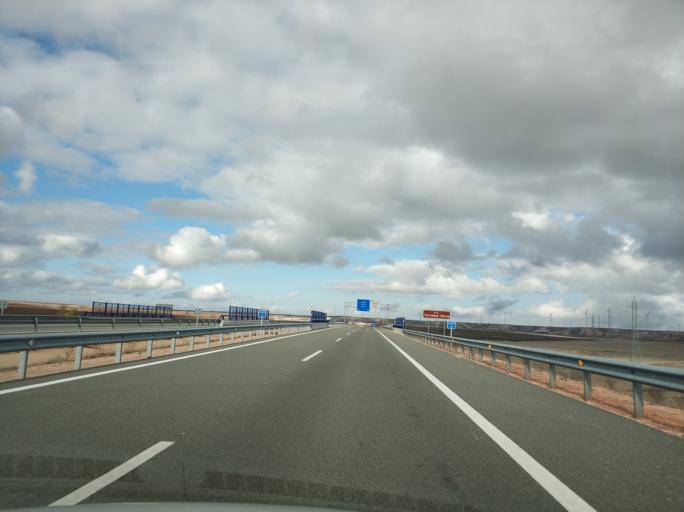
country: ES
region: Castille and Leon
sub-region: Provincia de Soria
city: Alcubilla de las Penas
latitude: 41.2537
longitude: -2.4736
